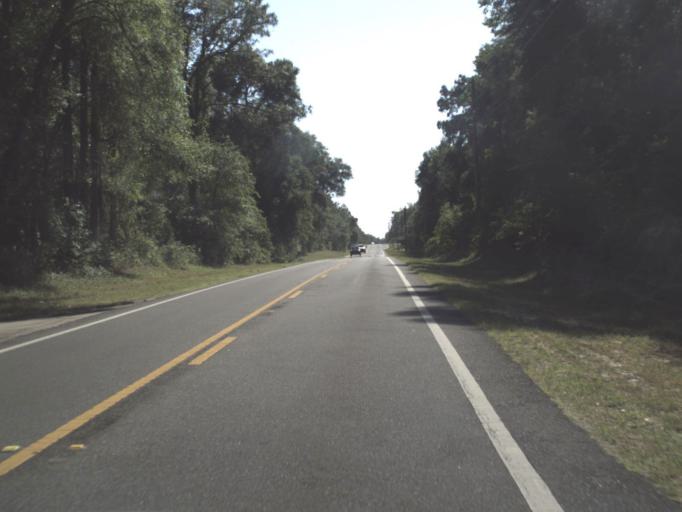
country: US
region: Florida
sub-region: Marion County
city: Dunnellon
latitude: 29.1372
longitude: -82.3922
